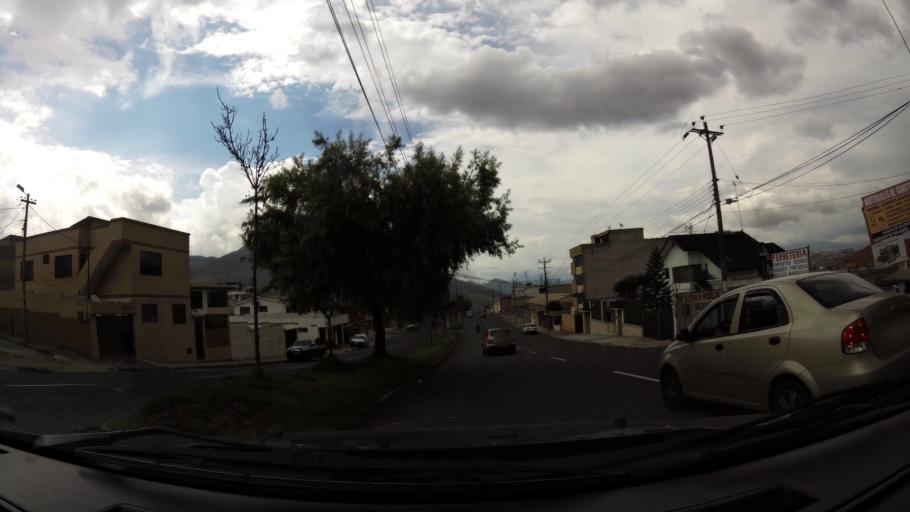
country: EC
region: Pichincha
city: Quito
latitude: -0.0891
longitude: -78.4672
